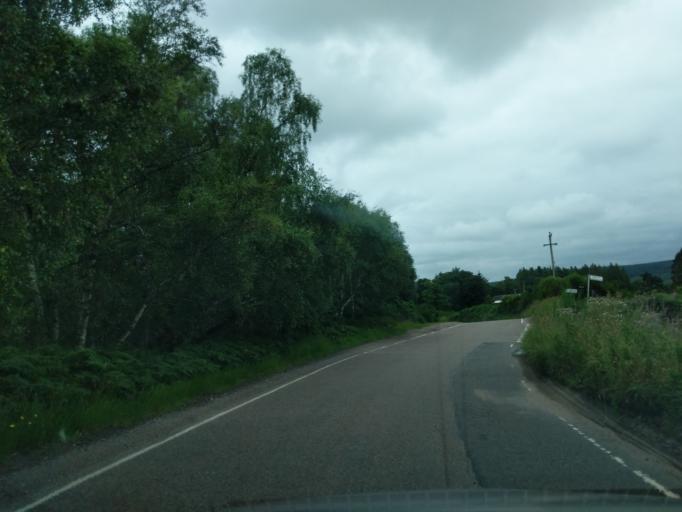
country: GB
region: Scotland
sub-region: Moray
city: Kinloss
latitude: 57.5746
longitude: -3.5445
